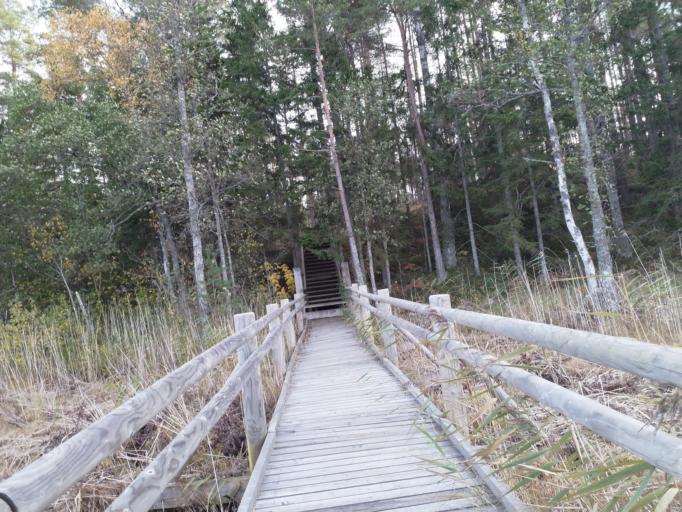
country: LV
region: Dundaga
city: Dundaga
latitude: 57.6516
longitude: 22.2580
